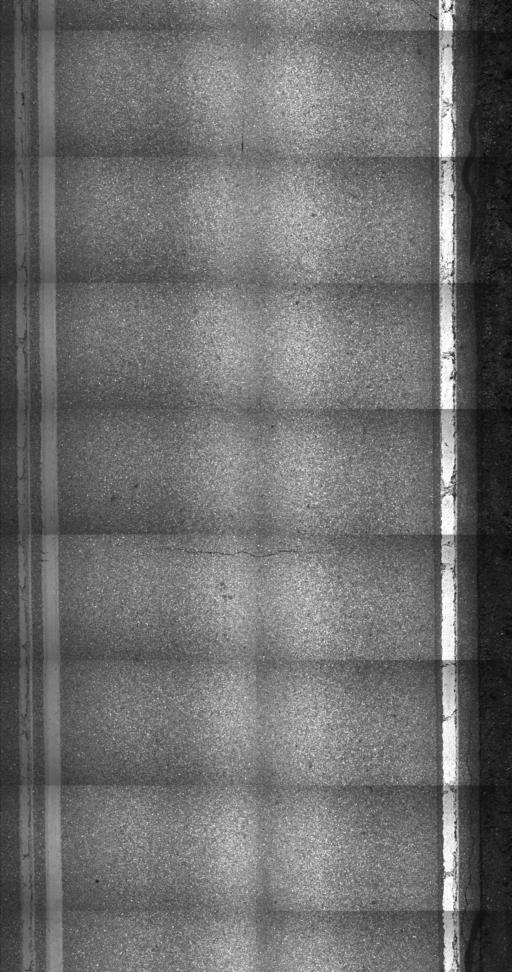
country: US
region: Vermont
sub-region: Bennington County
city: Arlington
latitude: 43.0958
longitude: -73.1398
